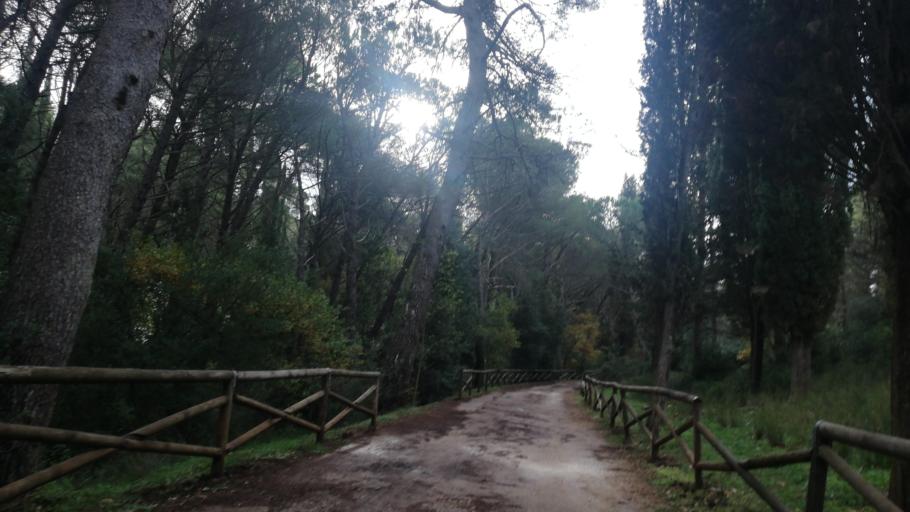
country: IT
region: Apulia
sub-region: Provincia di Bari
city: Cassano delle Murge
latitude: 40.8883
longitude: 16.7009
